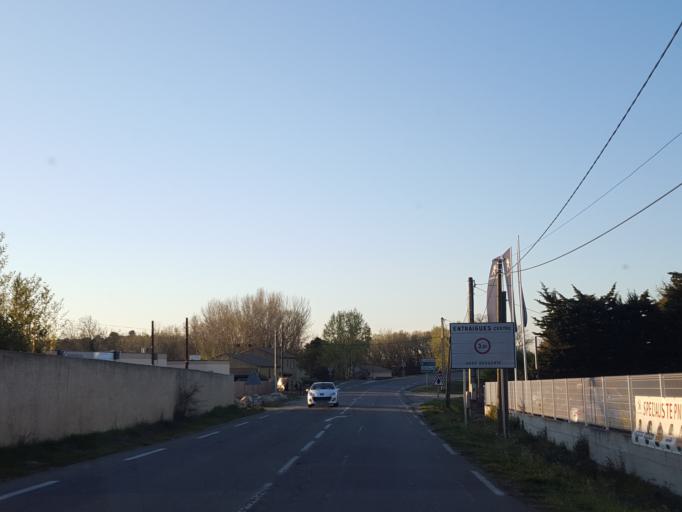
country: FR
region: Provence-Alpes-Cote d'Azur
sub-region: Departement du Vaucluse
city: Entraigues-sur-la-Sorgue
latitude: 43.9909
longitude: 4.9134
